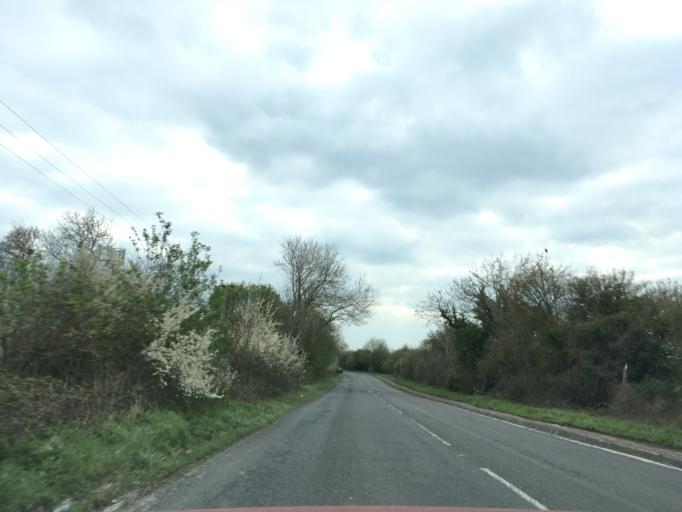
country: GB
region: England
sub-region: Oxfordshire
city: Carterton
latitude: 51.7921
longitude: -1.5634
